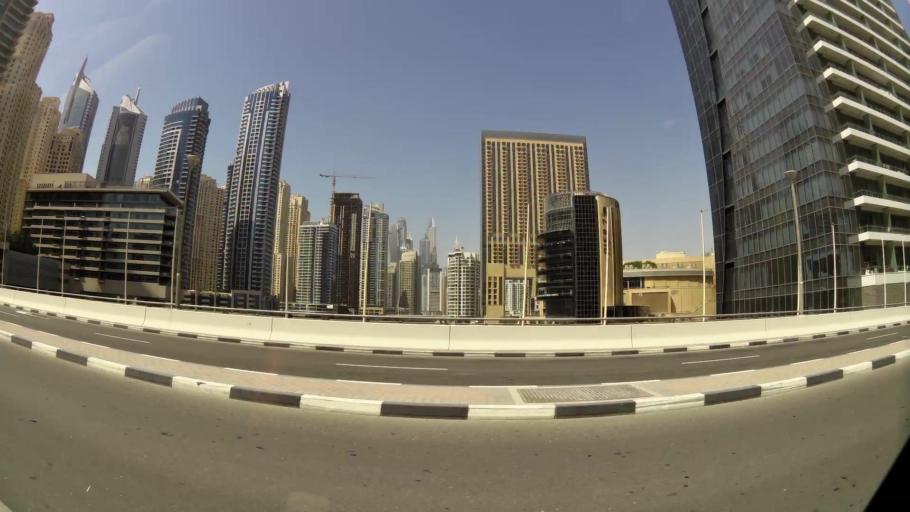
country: AE
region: Dubai
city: Dubai
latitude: 25.0752
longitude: 55.1371
